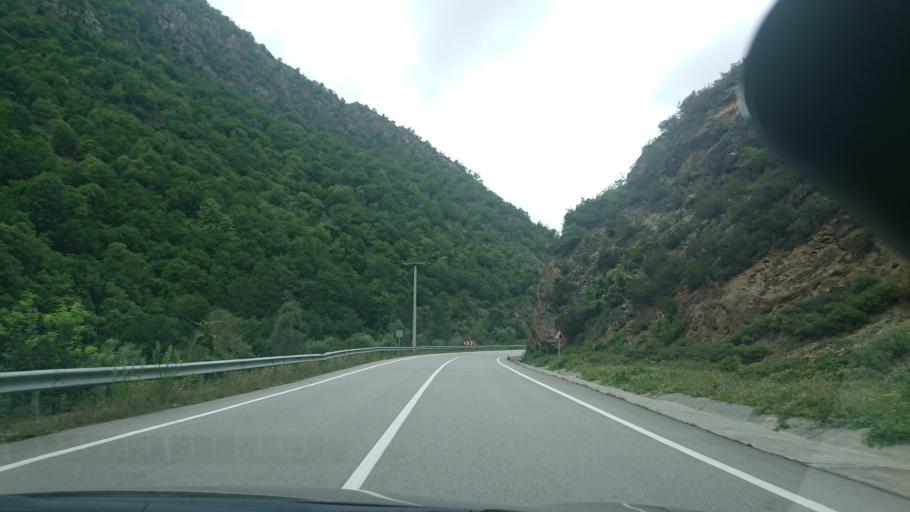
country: TR
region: Gumushane
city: Kurtun
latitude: 40.7319
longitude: 39.0114
